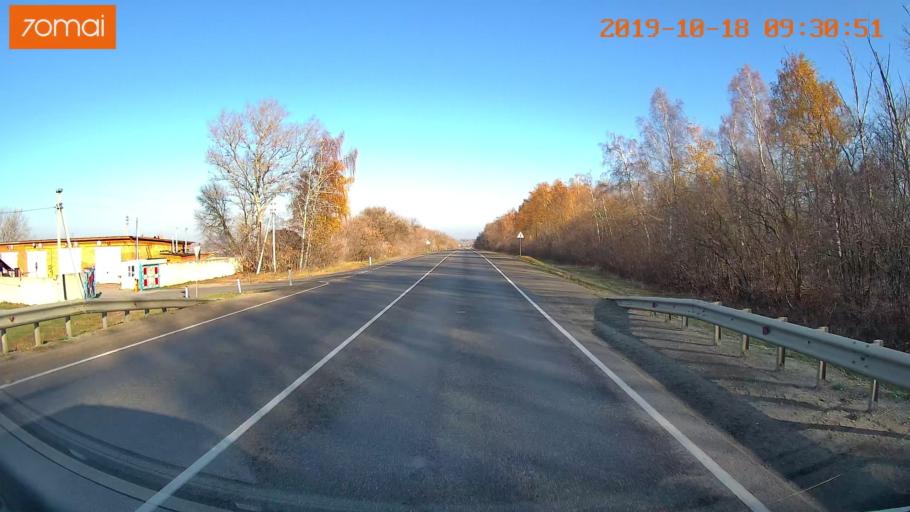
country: RU
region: Tula
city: Yefremov
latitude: 53.1432
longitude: 38.1591
